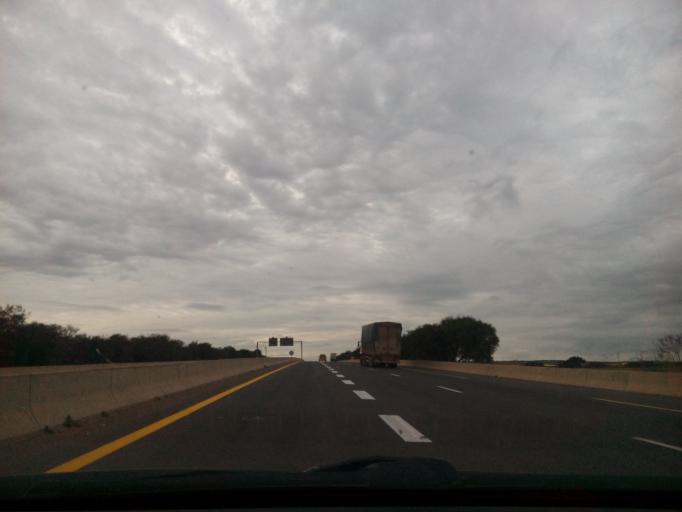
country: DZ
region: Mascara
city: Sig
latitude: 35.5420
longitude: -0.3468
